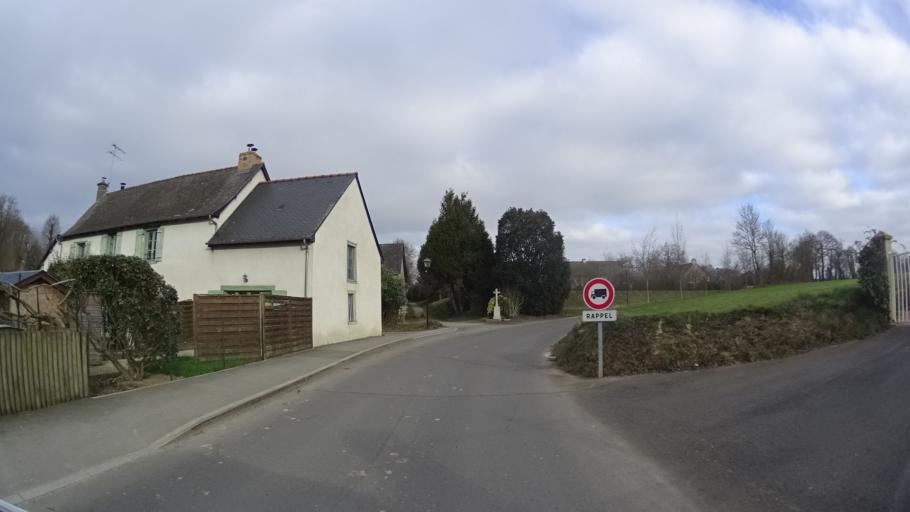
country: FR
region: Brittany
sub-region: Departement d'Ille-et-Vilaine
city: Saint-Gilles
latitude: 48.1784
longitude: -1.8530
